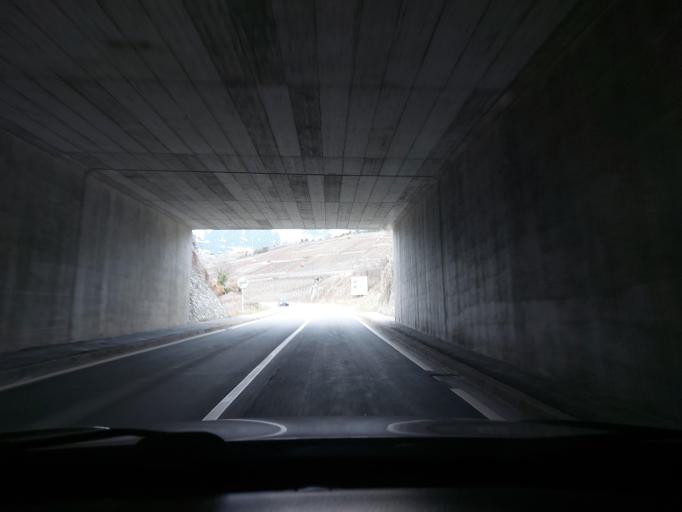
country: CH
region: Valais
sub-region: Sion District
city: Saviese
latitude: 46.2357
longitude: 7.3385
